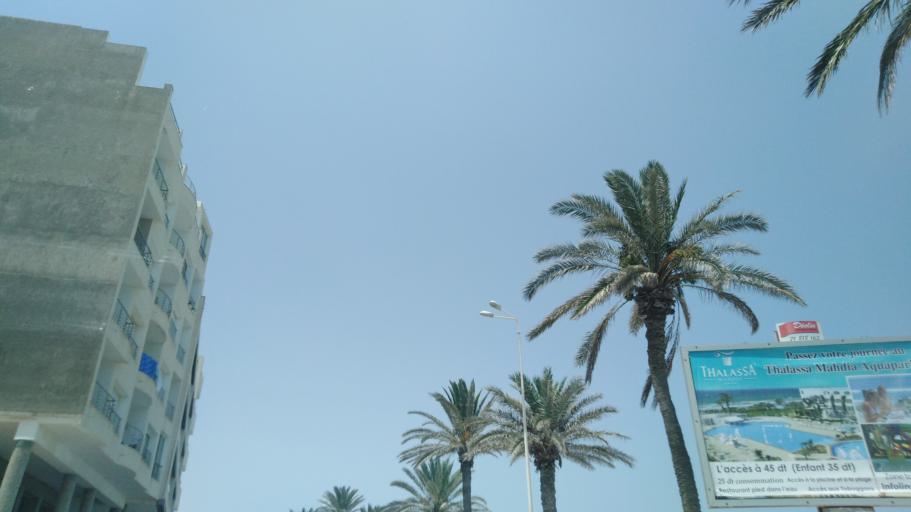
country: TN
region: Al Mahdiyah
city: Mahdia
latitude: 35.5229
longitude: 11.0413
